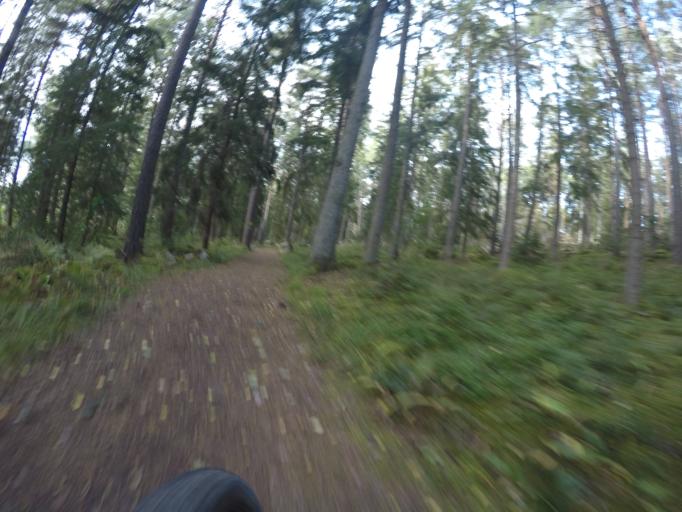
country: SE
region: Vaestmanland
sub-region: Kopings Kommun
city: Koping
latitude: 59.5288
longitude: 15.9982
